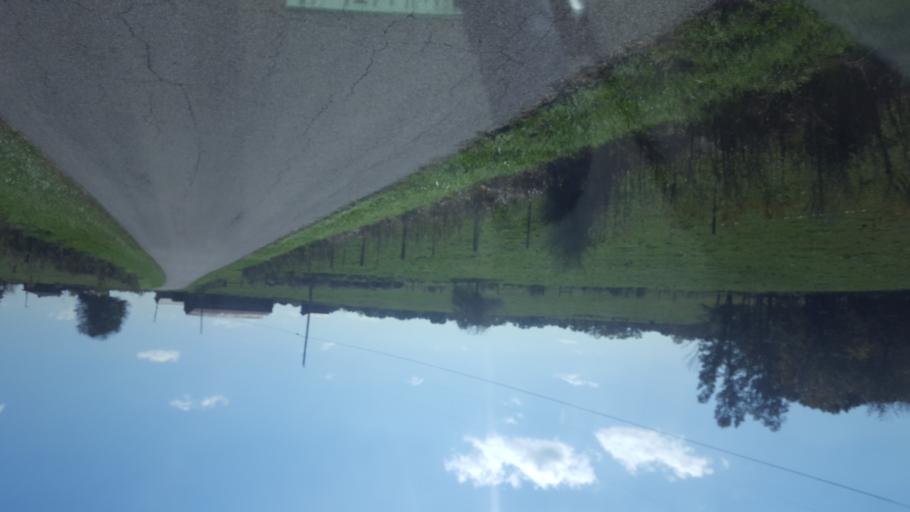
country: US
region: Kentucky
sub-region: Fleming County
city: Flemingsburg
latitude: 38.4595
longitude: -83.5288
